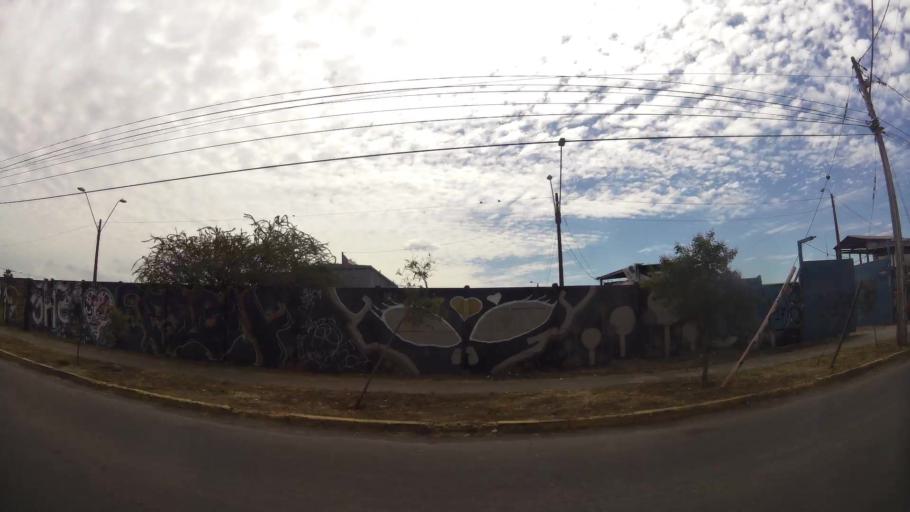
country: CL
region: Santiago Metropolitan
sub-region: Provincia de Santiago
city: La Pintana
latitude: -33.5846
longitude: -70.6314
